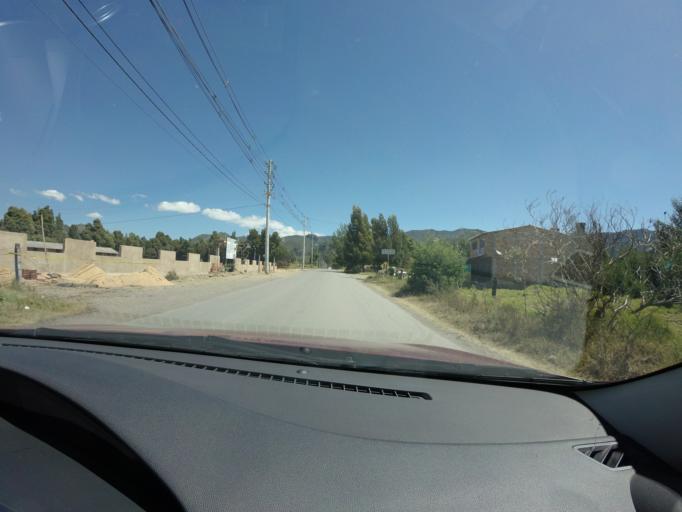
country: CO
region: Cundinamarca
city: Cucunuba
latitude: 5.2523
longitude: -73.7780
